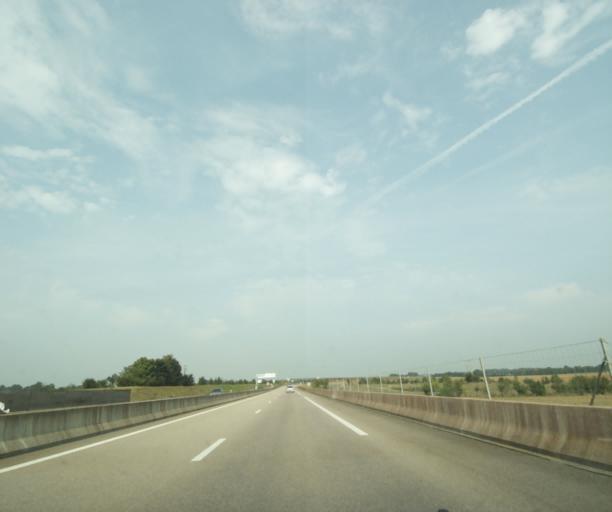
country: FR
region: Lower Normandy
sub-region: Departement du Calvados
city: Falaise
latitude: 48.8709
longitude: -0.2093
